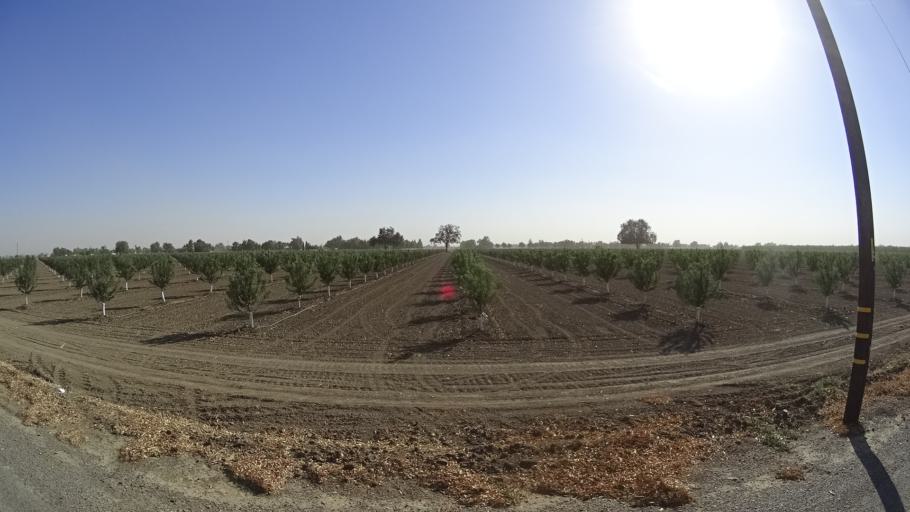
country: US
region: California
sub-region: Yolo County
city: Woodland
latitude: 38.7496
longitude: -121.7835
